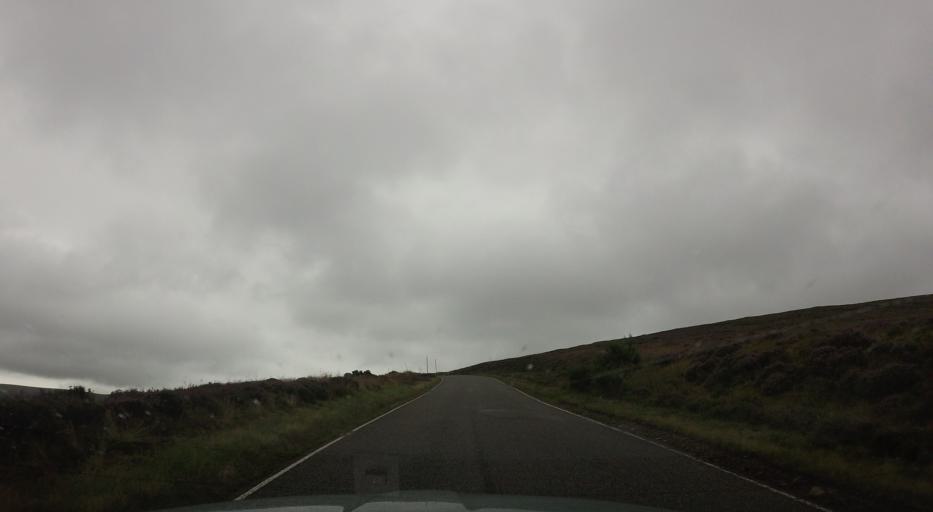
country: GB
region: Scotland
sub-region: Aberdeenshire
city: Banchory
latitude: 56.9365
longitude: -2.5728
